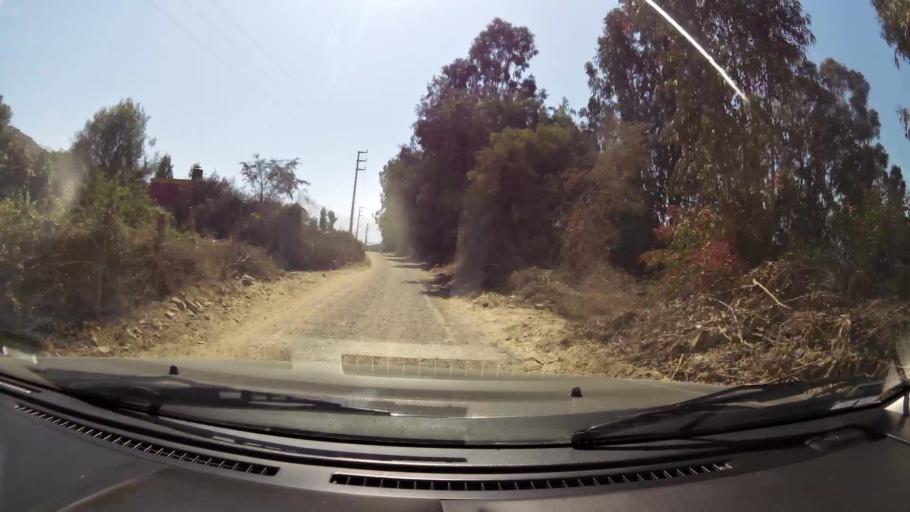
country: PE
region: Ica
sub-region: Provincia de Ica
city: Guadalupe
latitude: -13.8767
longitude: -75.6432
